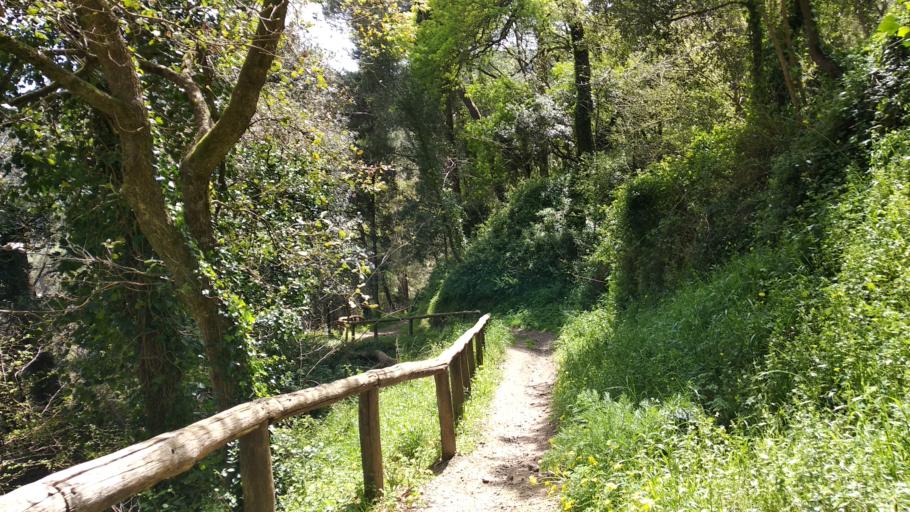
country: IT
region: Sicily
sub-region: Messina
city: Castanea delle Furie
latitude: 38.2147
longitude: 15.5071
